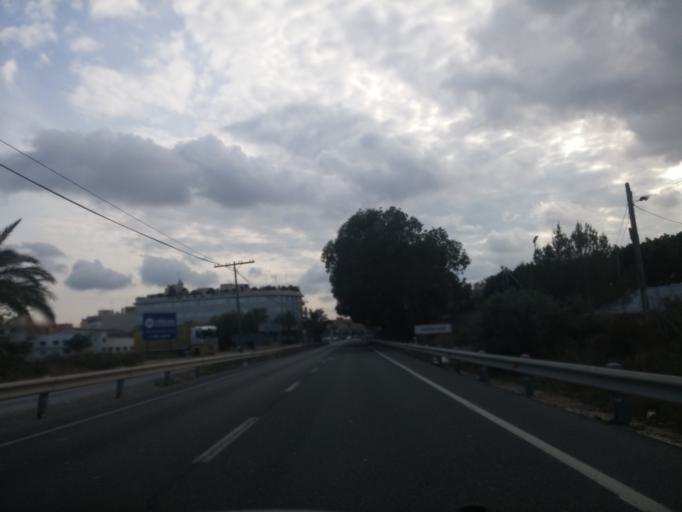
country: ES
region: Valencia
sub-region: Provincia de Alicante
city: Santa Pola
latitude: 38.2951
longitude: -0.5834
